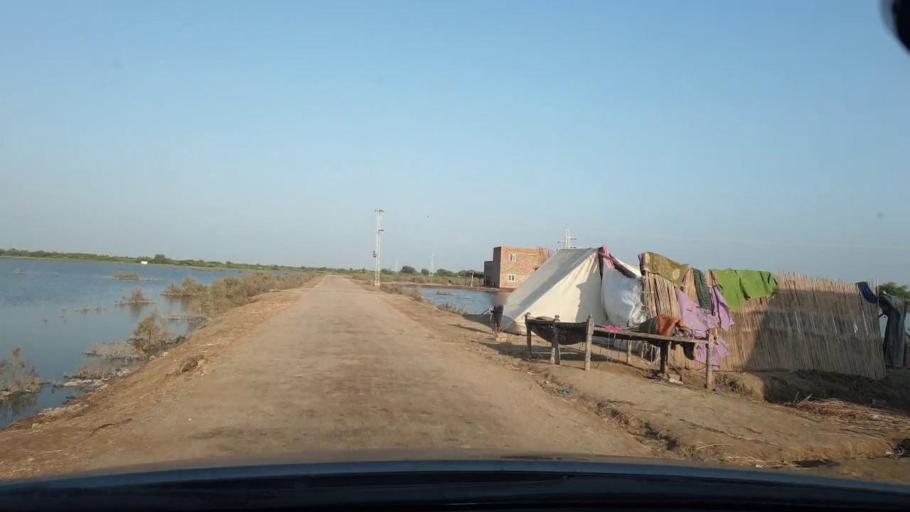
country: PK
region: Sindh
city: Naukot
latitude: 24.7699
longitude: 69.2001
